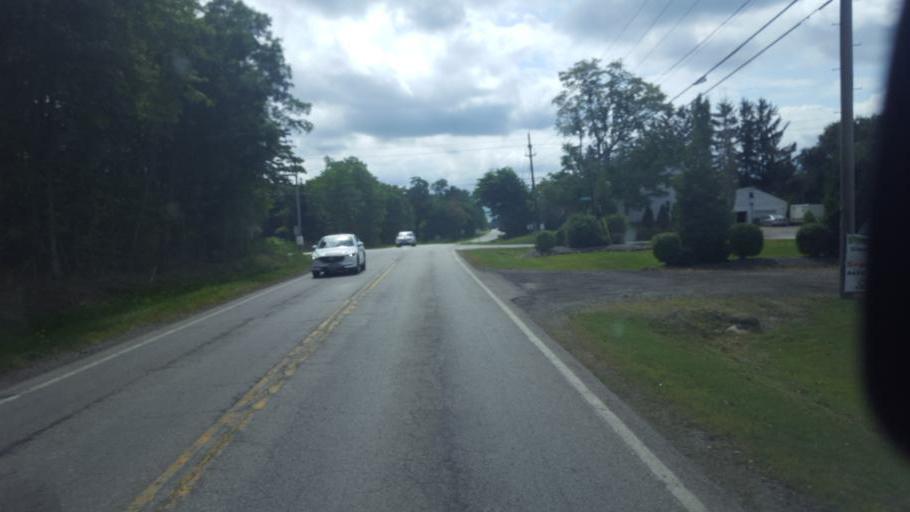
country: US
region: Ohio
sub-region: Lake County
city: Perry
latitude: 41.7015
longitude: -81.1760
